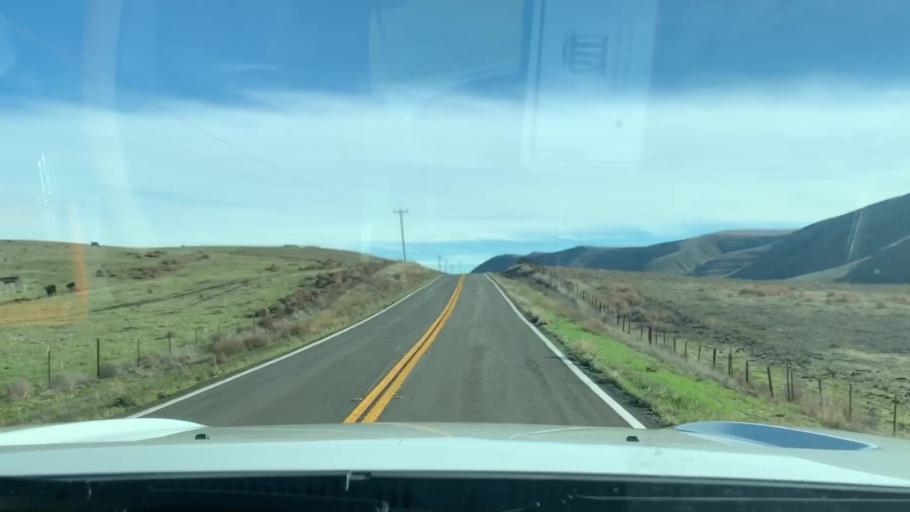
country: US
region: California
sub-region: Monterey County
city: King City
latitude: 36.1515
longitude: -120.9288
